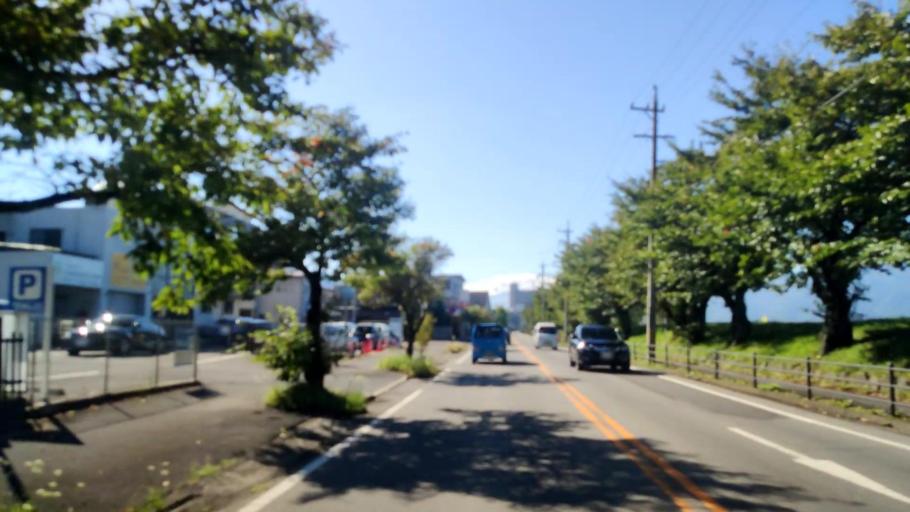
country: JP
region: Nagano
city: Suwa
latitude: 36.0584
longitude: 138.1103
